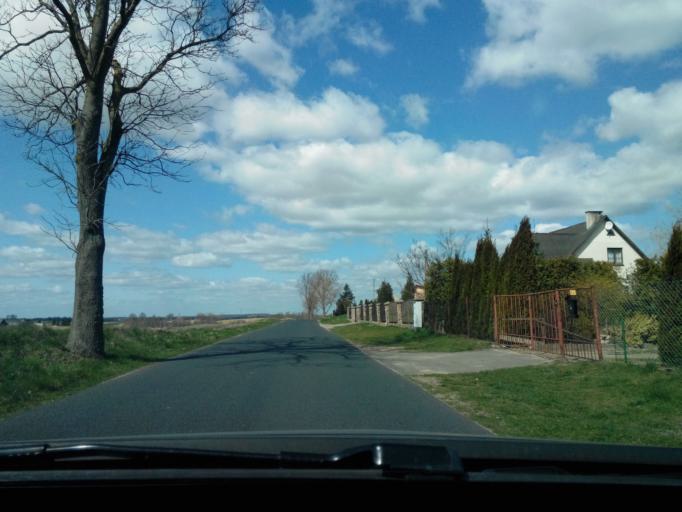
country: PL
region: Warmian-Masurian Voivodeship
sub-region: Powiat nowomiejski
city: Biskupiec
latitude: 53.4591
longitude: 19.3237
